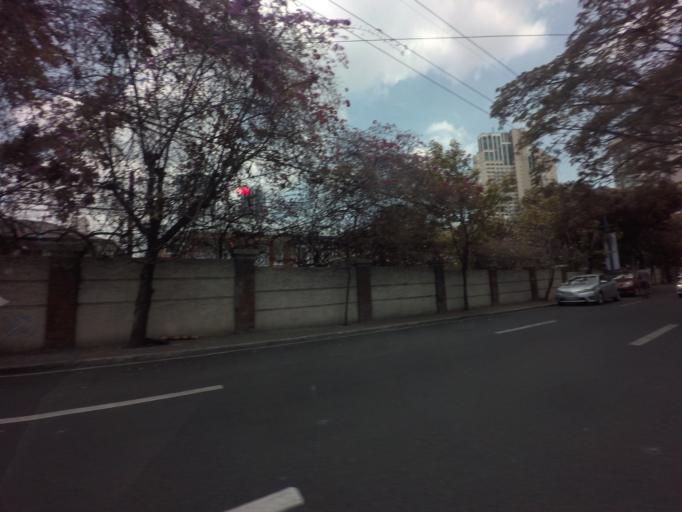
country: PH
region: Metro Manila
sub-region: Makati City
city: Makati City
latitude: 14.5625
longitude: 121.0320
